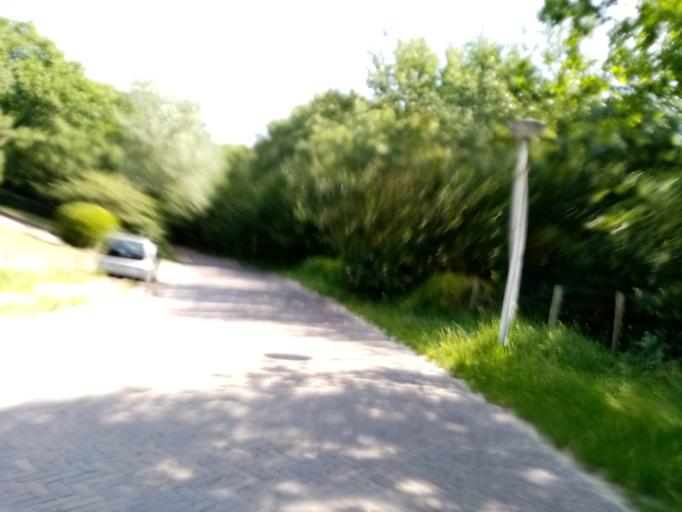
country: NL
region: South Holland
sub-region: Gemeente Noordwijk
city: Noordwijk-Binnen
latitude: 52.2346
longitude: 4.4315
